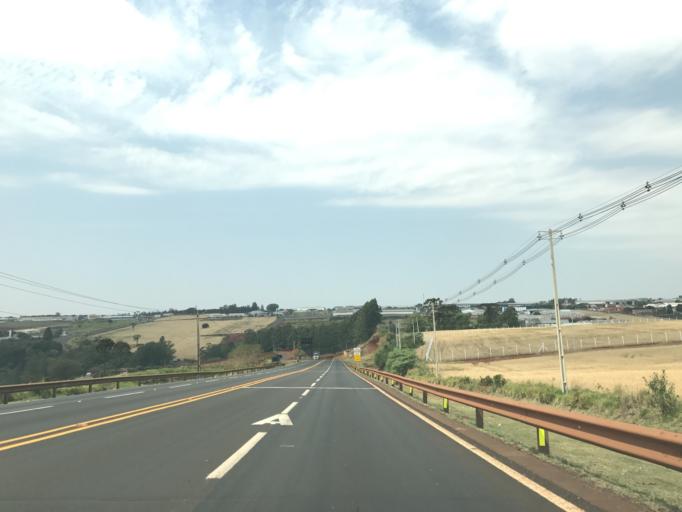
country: BR
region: Parana
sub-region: Arapongas
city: Arapongas
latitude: -23.3740
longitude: -51.4340
